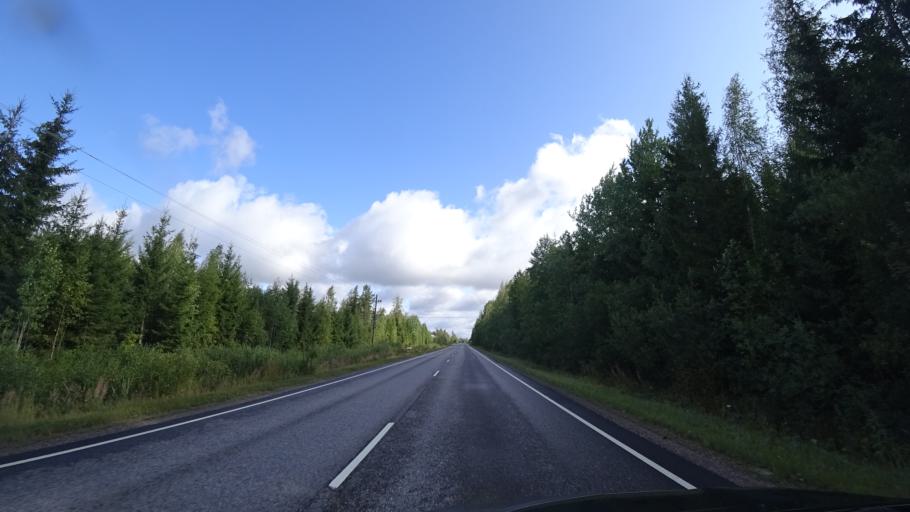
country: FI
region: Uusimaa
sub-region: Helsinki
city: Hyvinge
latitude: 60.5445
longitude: 24.9350
